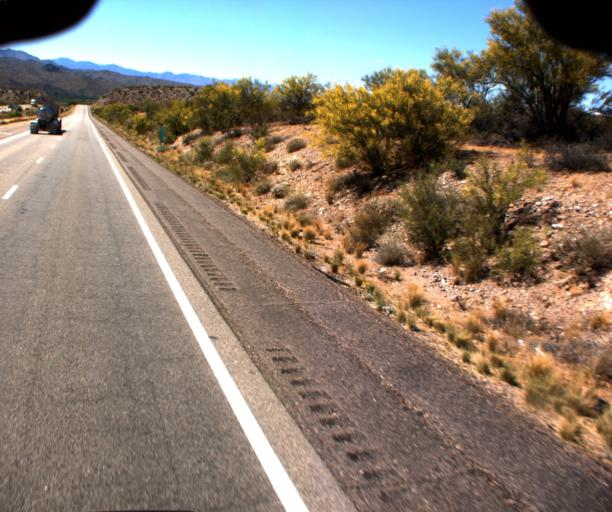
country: US
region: Arizona
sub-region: Yavapai County
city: Bagdad
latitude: 34.6321
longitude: -113.5471
